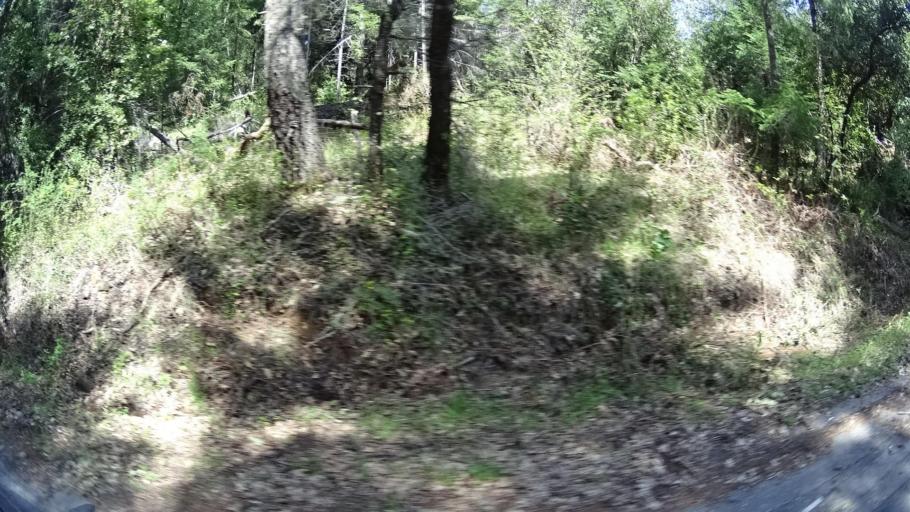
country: US
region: California
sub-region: Humboldt County
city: Redway
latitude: 40.2805
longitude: -123.6431
